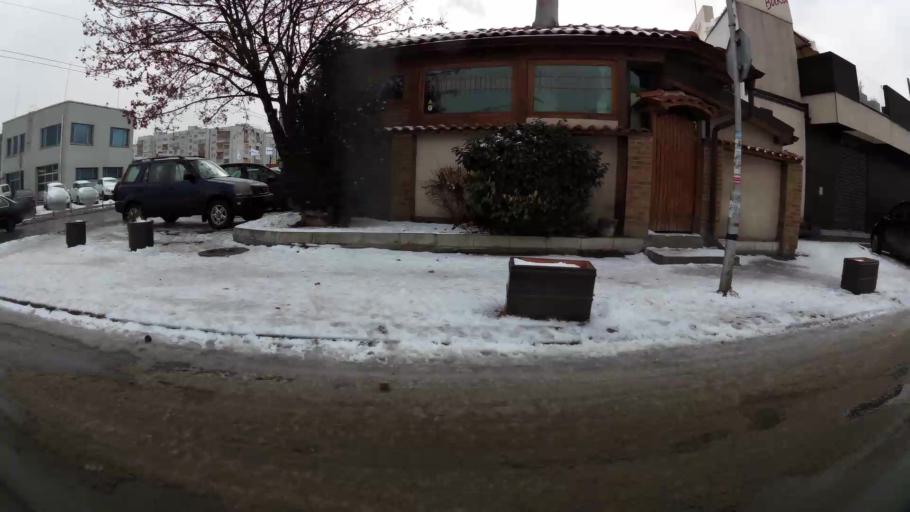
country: BG
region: Sofia-Capital
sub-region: Stolichna Obshtina
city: Sofia
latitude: 42.7114
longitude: 23.3799
